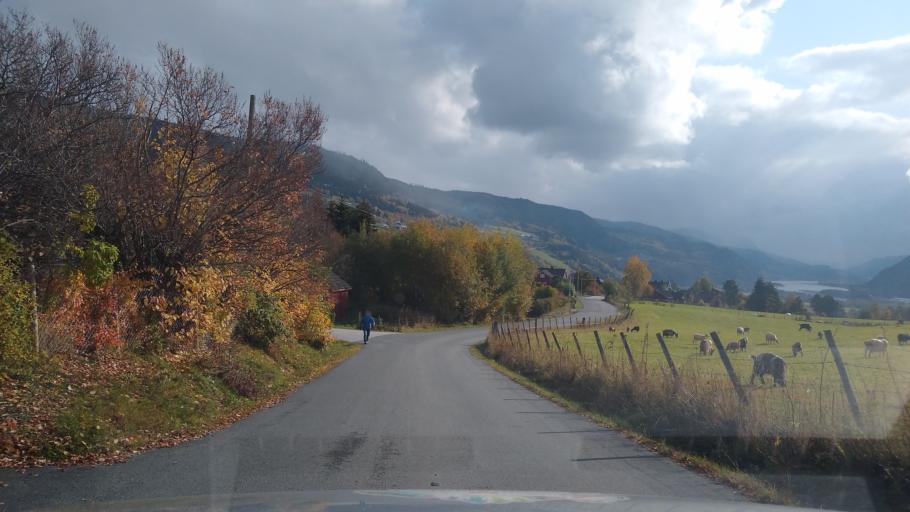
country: NO
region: Oppland
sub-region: Ringebu
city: Ringebu
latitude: 61.5387
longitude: 10.1343
